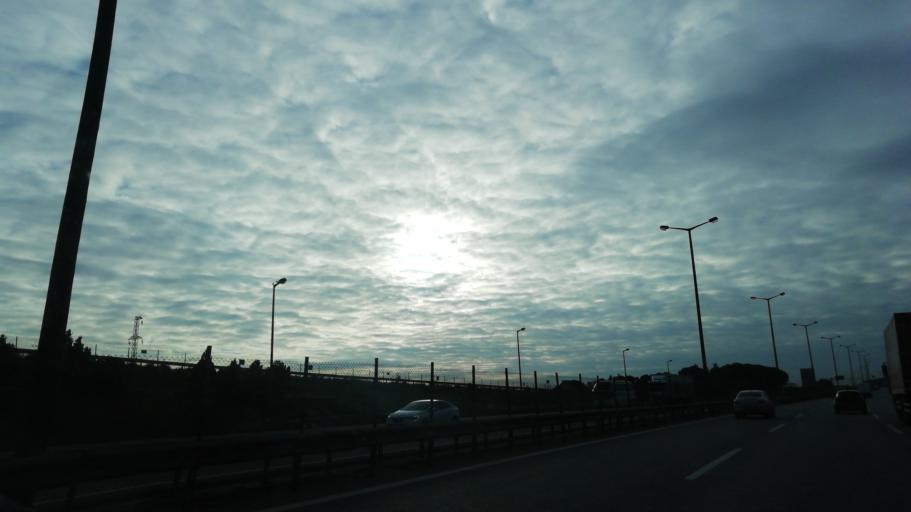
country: TR
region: Istanbul
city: Sultanbeyli
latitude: 40.9246
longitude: 29.3504
